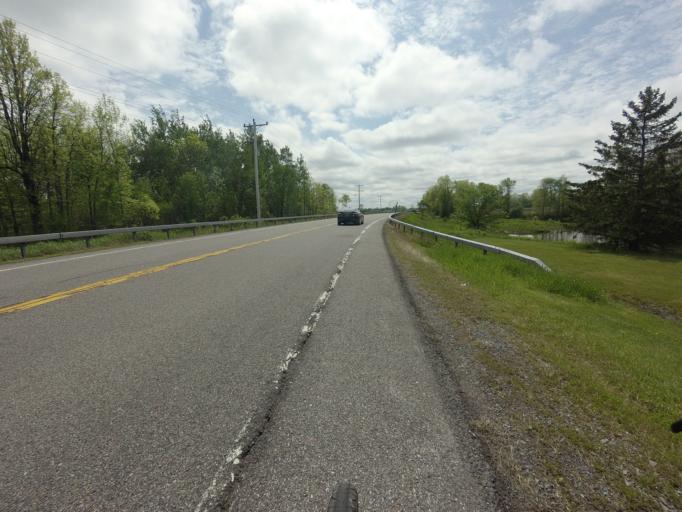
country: CA
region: Ontario
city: Cornwall
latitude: 44.9604
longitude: -74.6674
